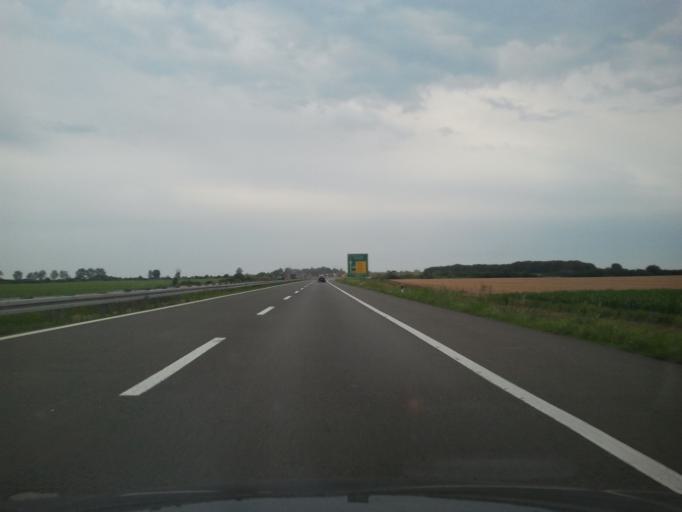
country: RS
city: Sasinci
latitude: 44.9667
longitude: 19.7900
